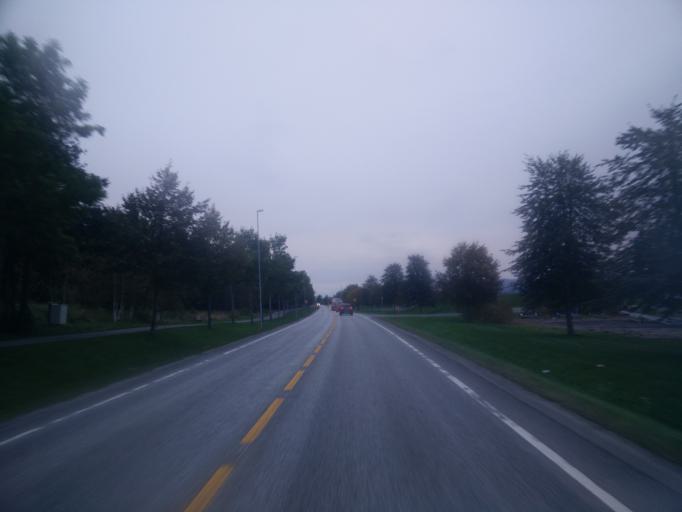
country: NO
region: More og Romsdal
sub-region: Molde
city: Molde
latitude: 62.7404
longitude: 7.2130
